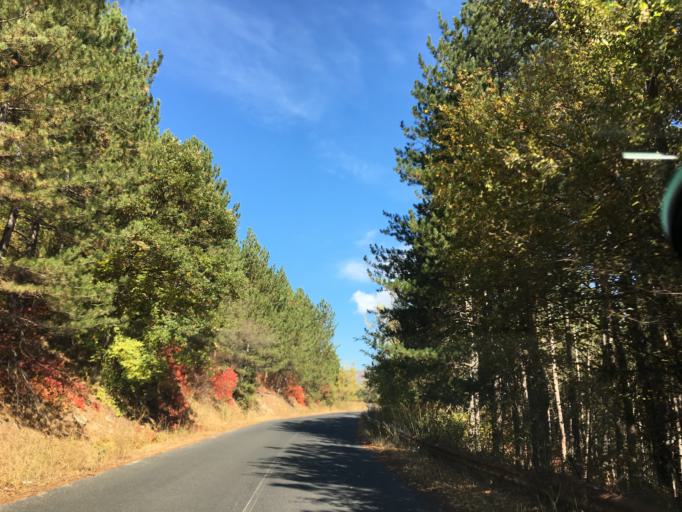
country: BG
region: Kurdzhali
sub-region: Obshtina Krumovgrad
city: Krumovgrad
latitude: 41.5511
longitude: 25.5572
